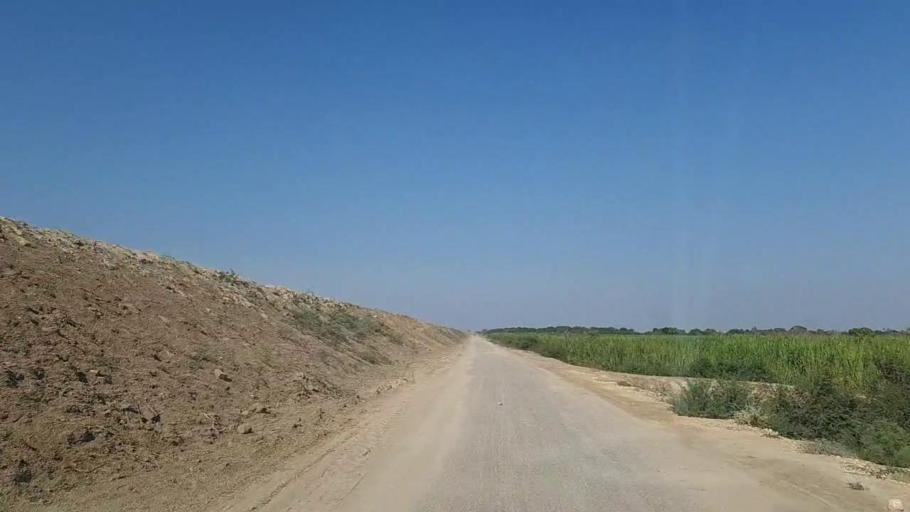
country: PK
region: Sindh
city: Chuhar Jamali
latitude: 24.5633
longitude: 68.0287
